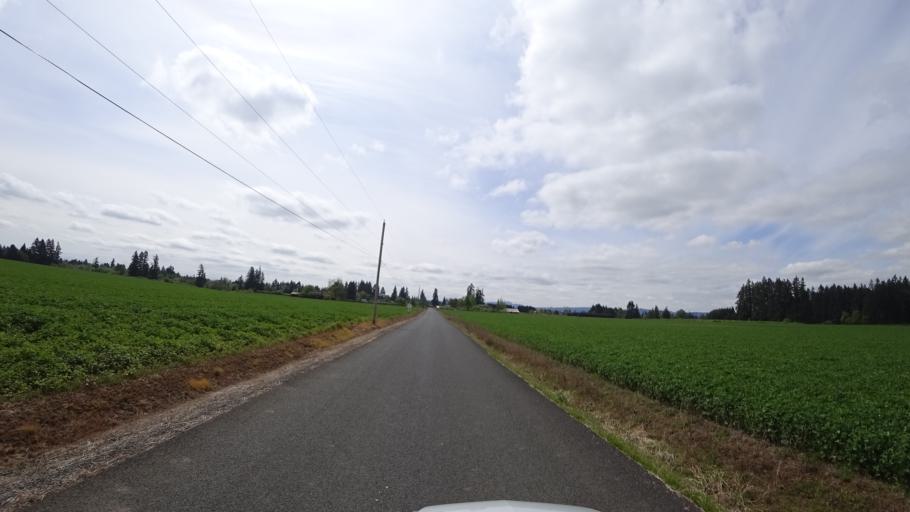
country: US
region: Oregon
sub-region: Washington County
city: Hillsboro
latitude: 45.5384
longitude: -123.0108
